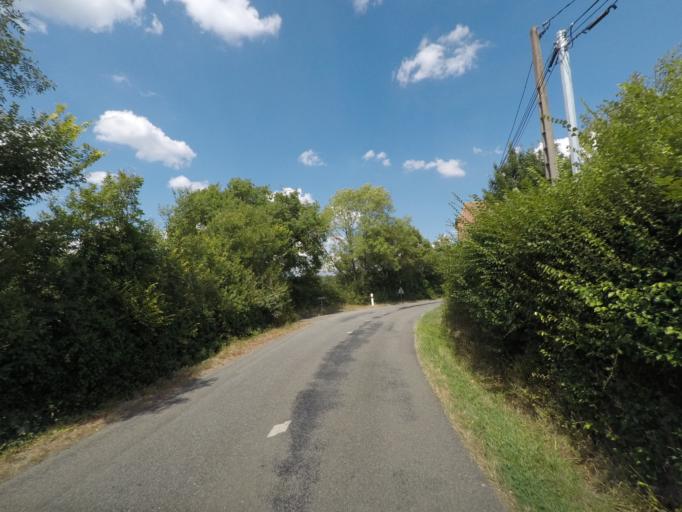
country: FR
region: Midi-Pyrenees
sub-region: Departement du Lot
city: Le Vigan
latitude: 44.5960
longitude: 1.5816
